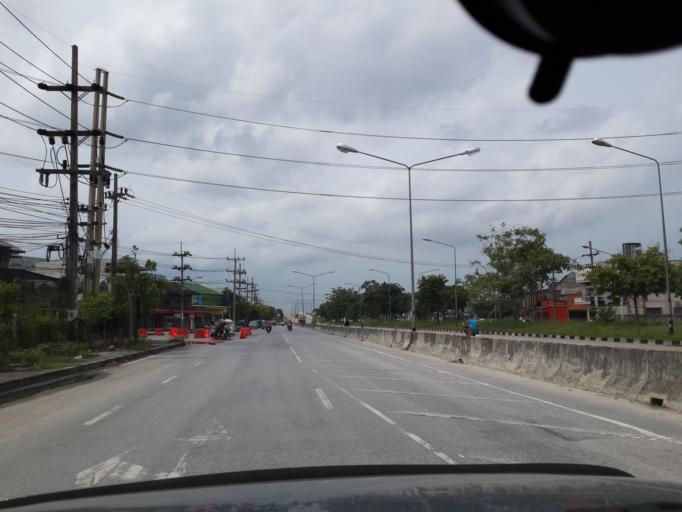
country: TH
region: Pattani
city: Pattani
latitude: 6.8514
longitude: 101.2549
